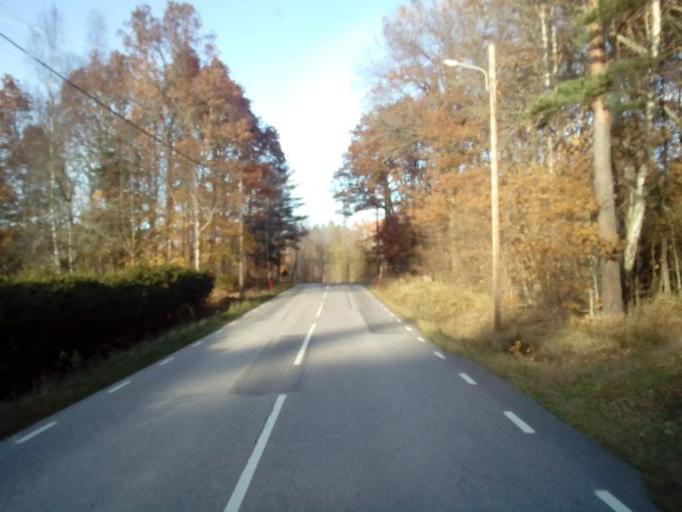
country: SE
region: Kalmar
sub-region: Vimmerby Kommun
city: Vimmerby
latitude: 57.7307
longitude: 16.0740
